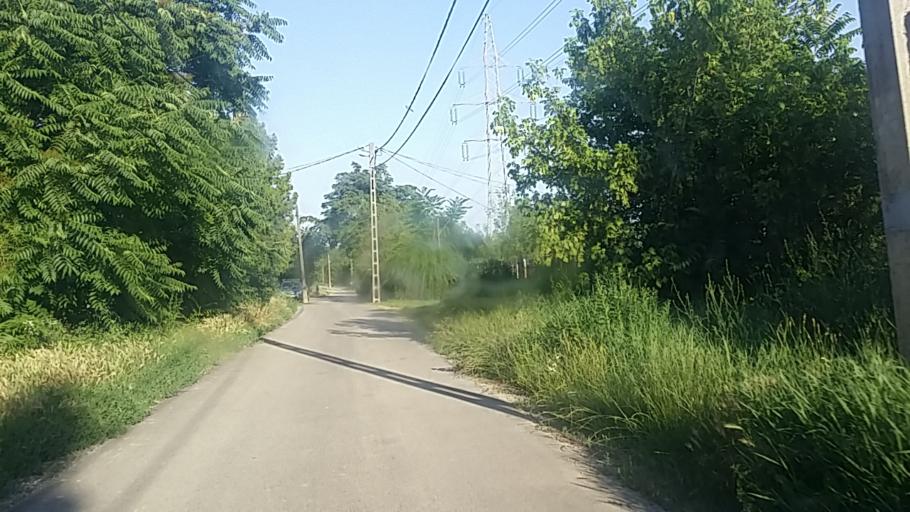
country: HU
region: Pest
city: Urom
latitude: 47.5792
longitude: 19.0150
